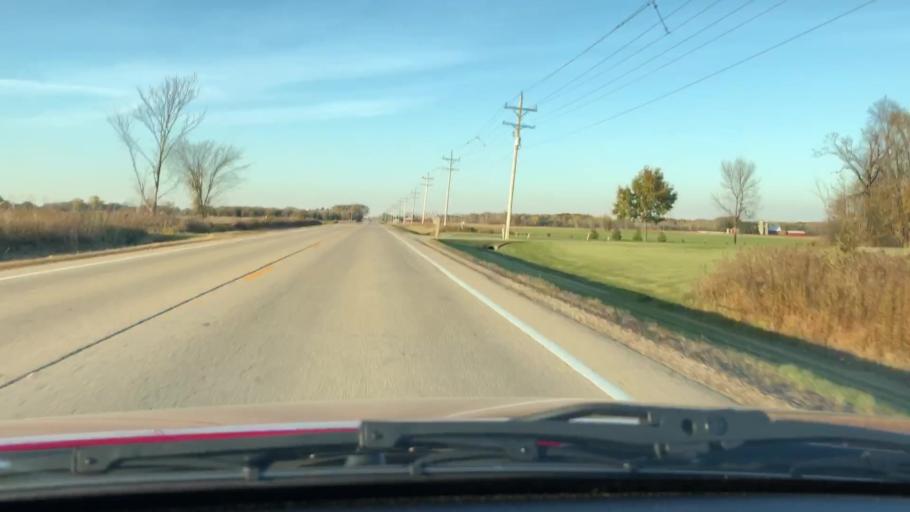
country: US
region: Wisconsin
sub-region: Outagamie County
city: Seymour
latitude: 44.4636
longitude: -88.2911
